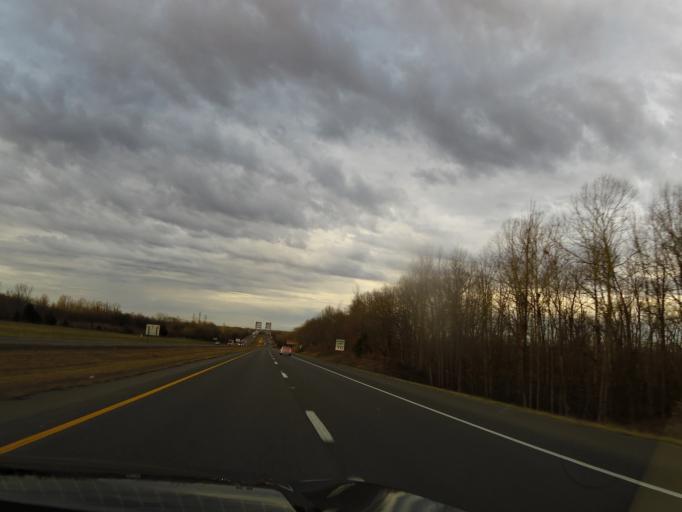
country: US
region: Kentucky
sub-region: Marshall County
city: Calvert City
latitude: 37.0350
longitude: -88.2759
